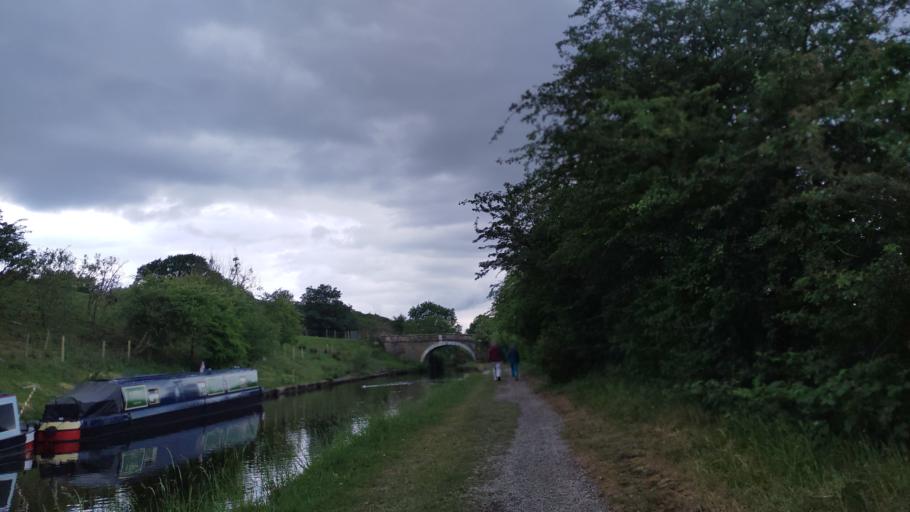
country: GB
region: England
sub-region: Lancashire
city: Chorley
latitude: 53.6950
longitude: -2.6040
